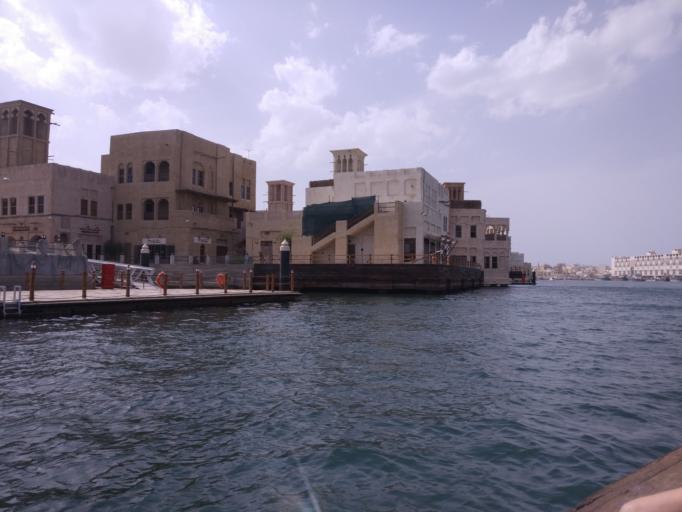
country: AE
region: Ash Shariqah
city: Sharjah
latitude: 25.2647
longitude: 55.3054
